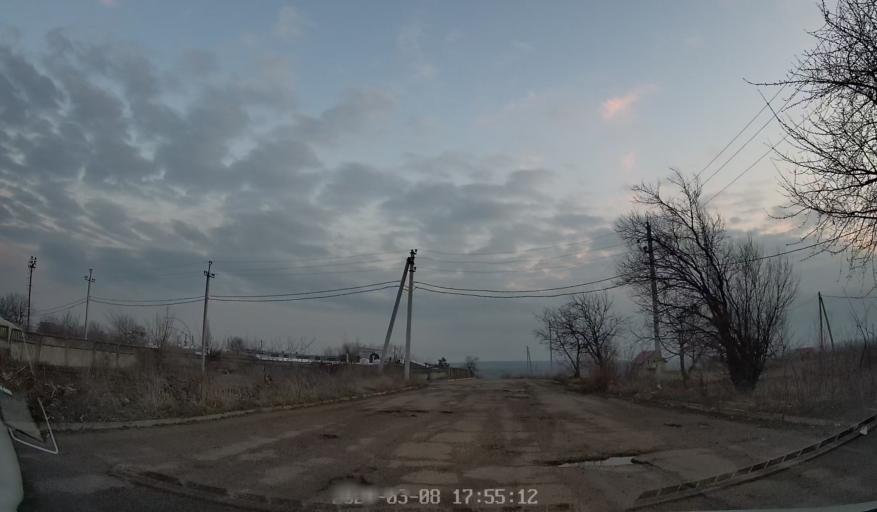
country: MD
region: Rezina
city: Rezina
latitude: 47.7521
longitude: 28.9490
